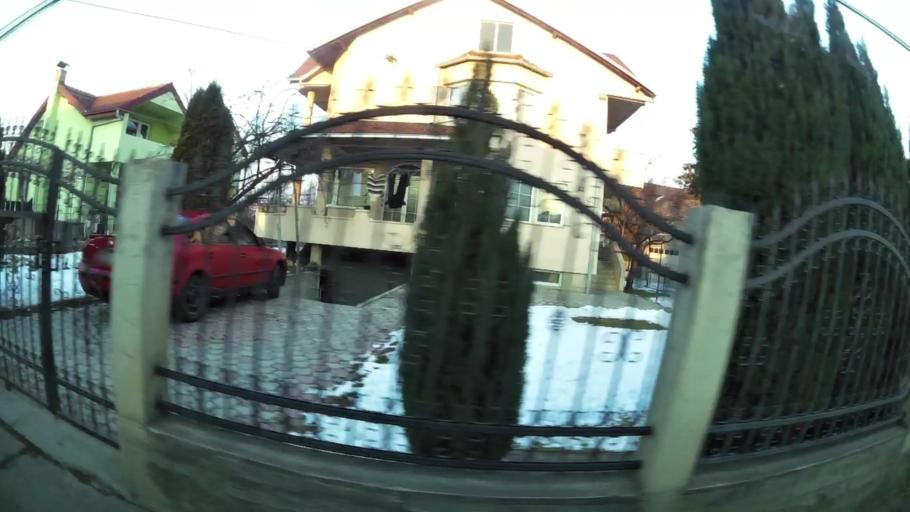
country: MK
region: Kisela Voda
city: Kisela Voda
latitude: 41.9801
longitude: 21.4902
